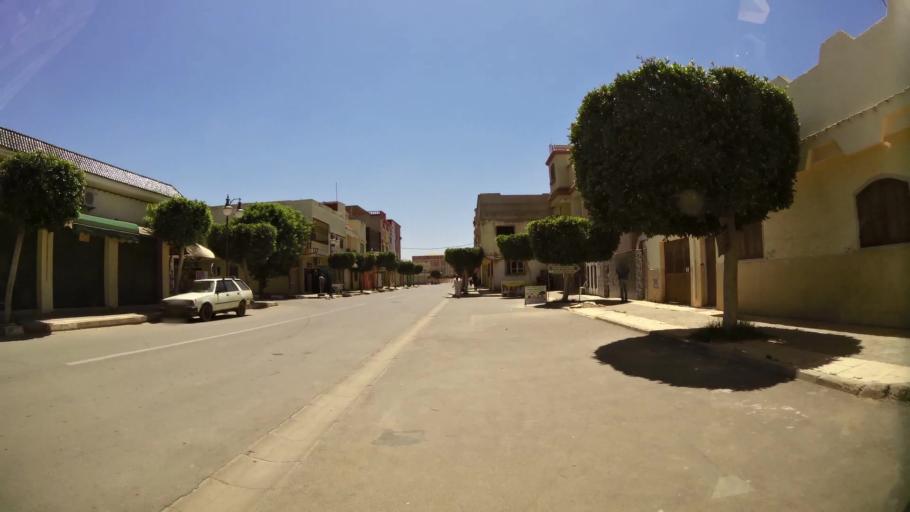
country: MA
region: Oriental
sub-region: Berkane-Taourirt
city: Madagh
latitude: 35.0797
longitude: -2.2175
